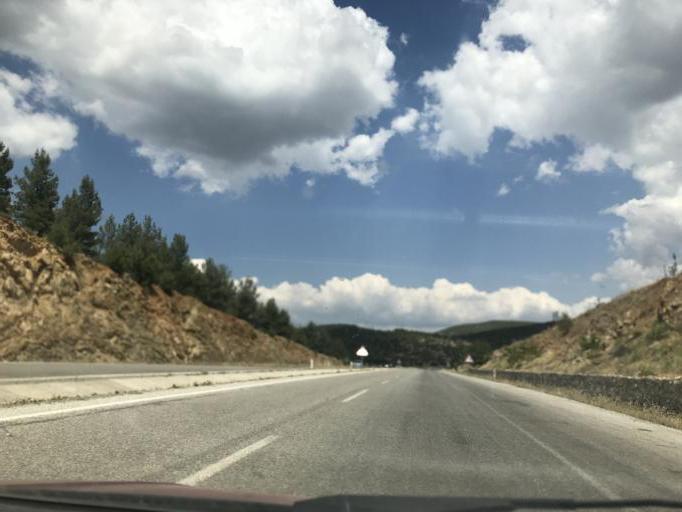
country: TR
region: Denizli
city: Tavas
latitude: 37.5815
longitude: 29.0941
